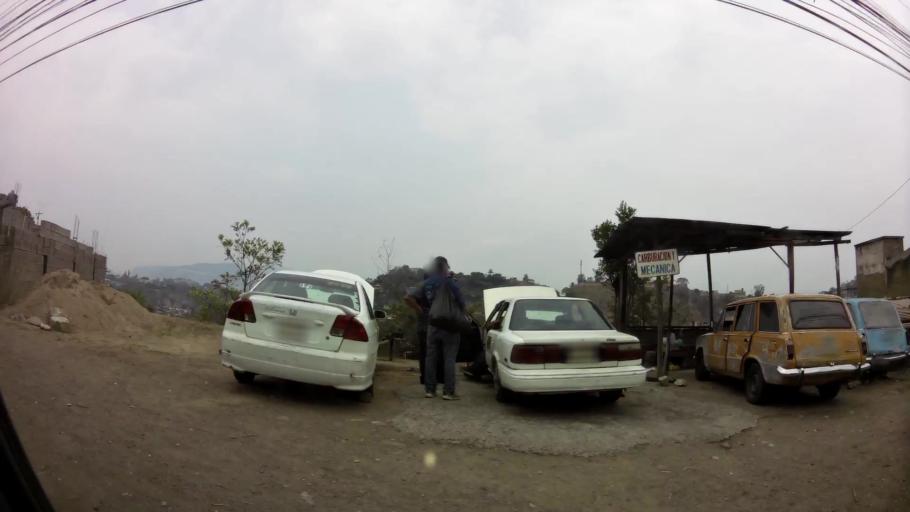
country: HN
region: Francisco Morazan
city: Tegucigalpa
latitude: 14.0794
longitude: -87.2258
